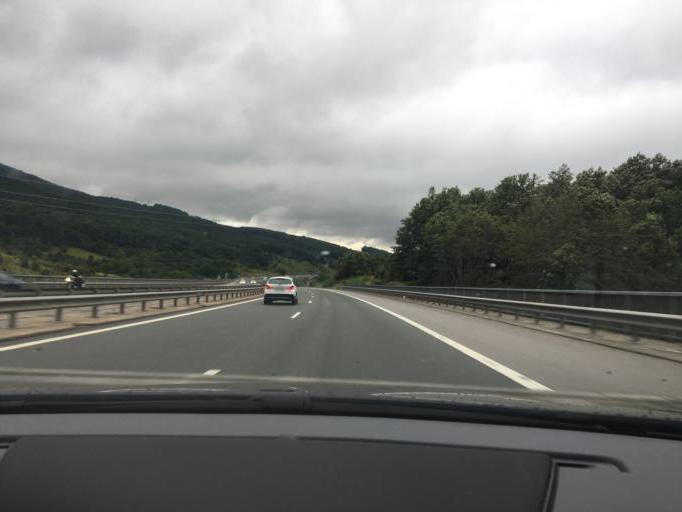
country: BG
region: Pernik
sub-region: Obshtina Pernik
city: Pernik
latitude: 42.6526
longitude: 23.1299
